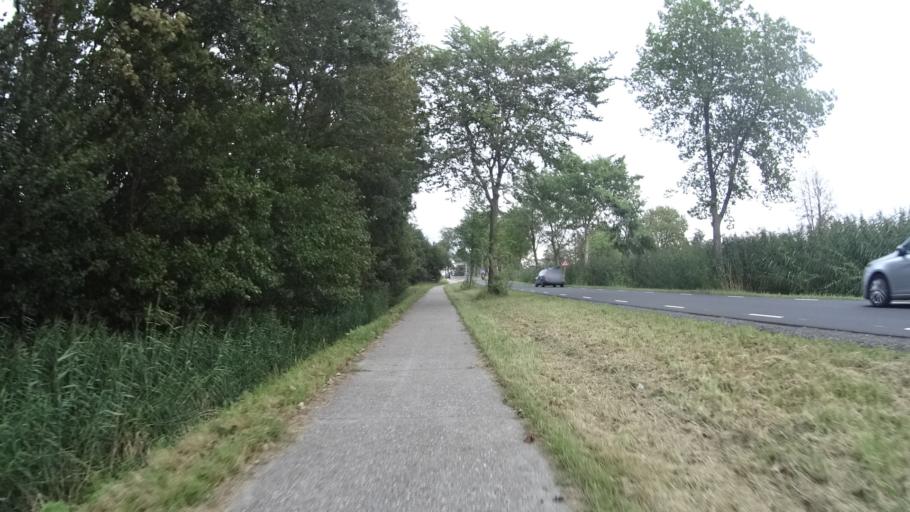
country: NL
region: Groningen
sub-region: Gemeente Groningen
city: Oosterpark
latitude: 53.2353
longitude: 6.6479
